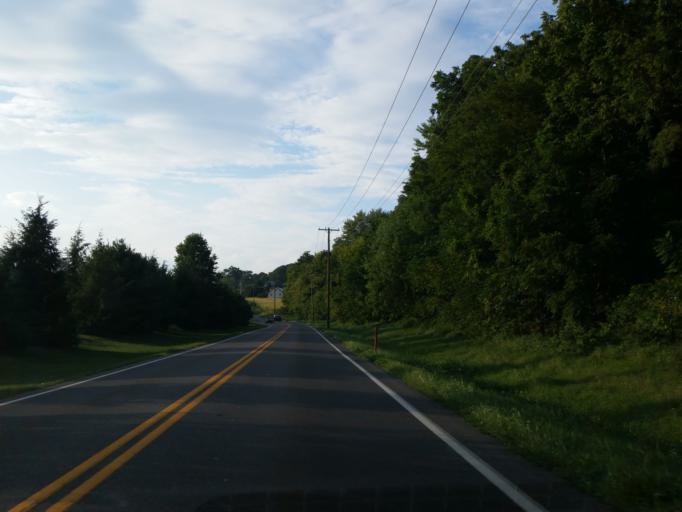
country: US
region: Pennsylvania
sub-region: Lebanon County
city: Palmyra
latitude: 40.3187
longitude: -76.5902
